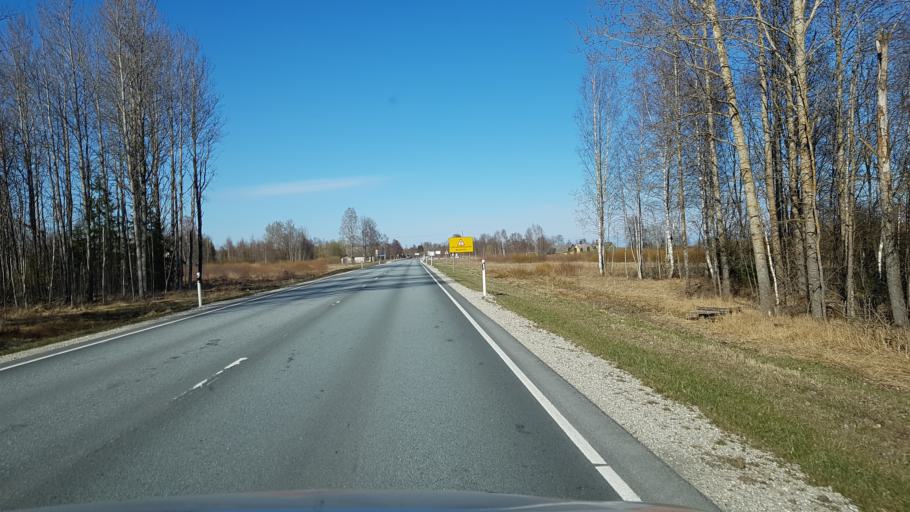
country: EE
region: Jogevamaa
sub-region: Mustvee linn
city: Mustvee
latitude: 58.8868
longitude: 26.9614
